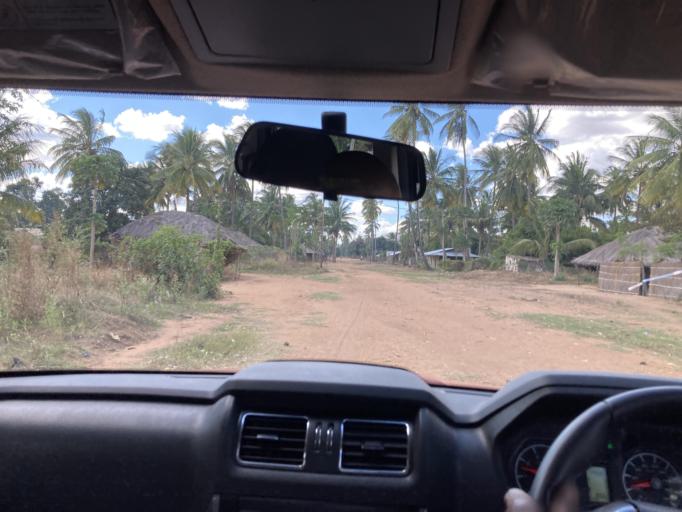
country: MZ
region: Cabo Delgado
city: Montepuez
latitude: -13.1429
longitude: 38.9972
